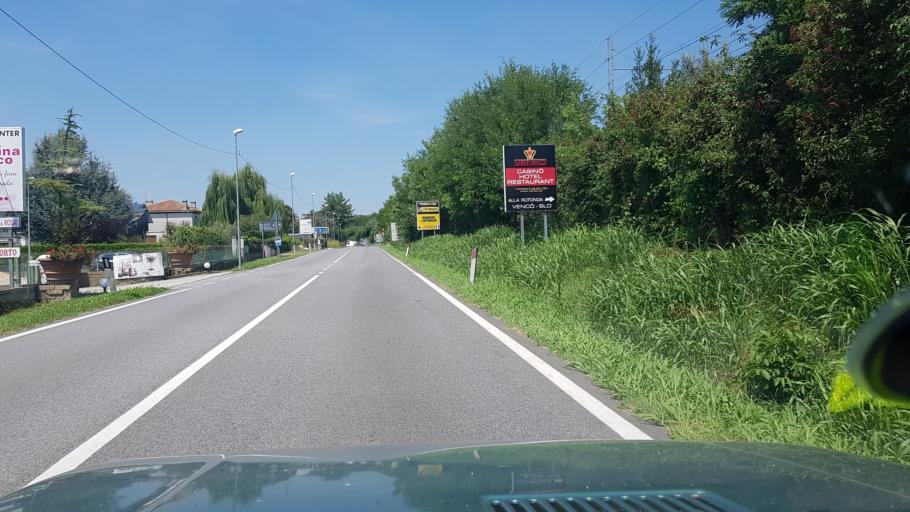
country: IT
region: Friuli Venezia Giulia
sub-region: Provincia di Gorizia
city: Cormons
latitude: 45.9510
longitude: 13.4740
